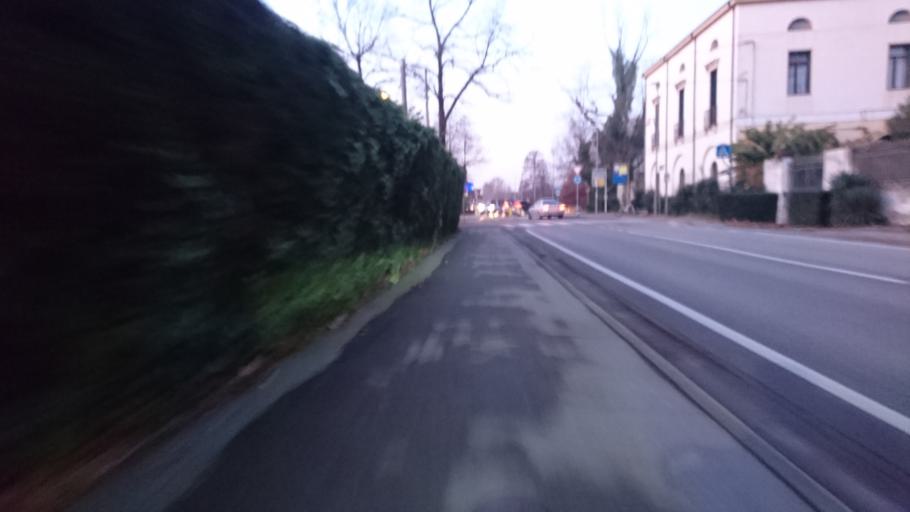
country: IT
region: Veneto
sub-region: Provincia di Padova
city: Albignasego
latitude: 45.3582
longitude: 11.8945
